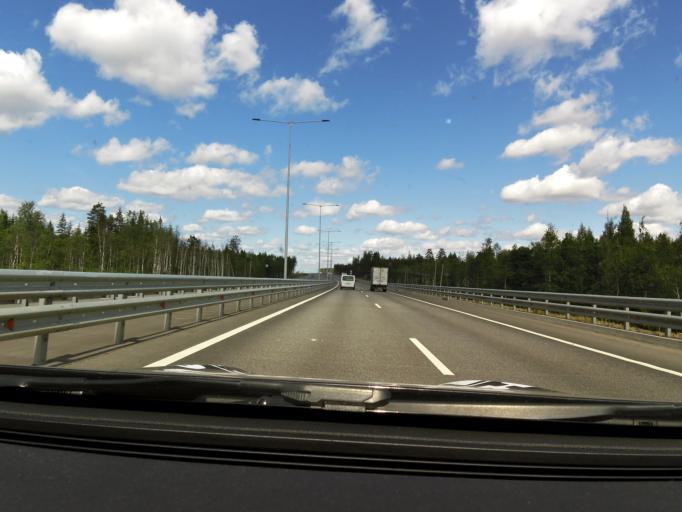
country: RU
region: Tverskaya
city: Krasnomayskiy
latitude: 57.6725
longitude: 34.2291
